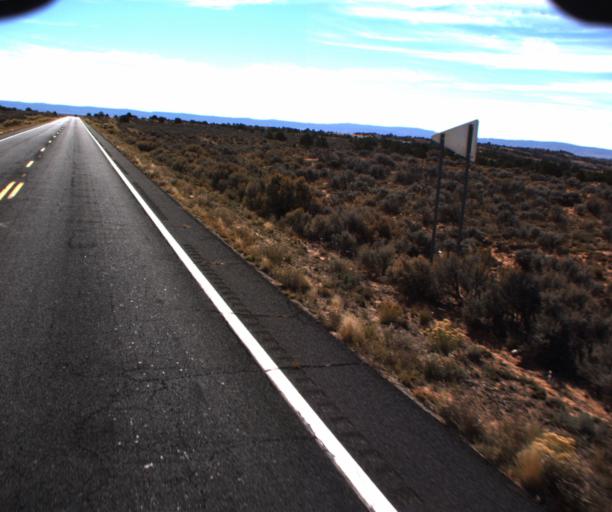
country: US
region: Arizona
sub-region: Coconino County
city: Kaibito
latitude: 36.5700
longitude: -110.7637
